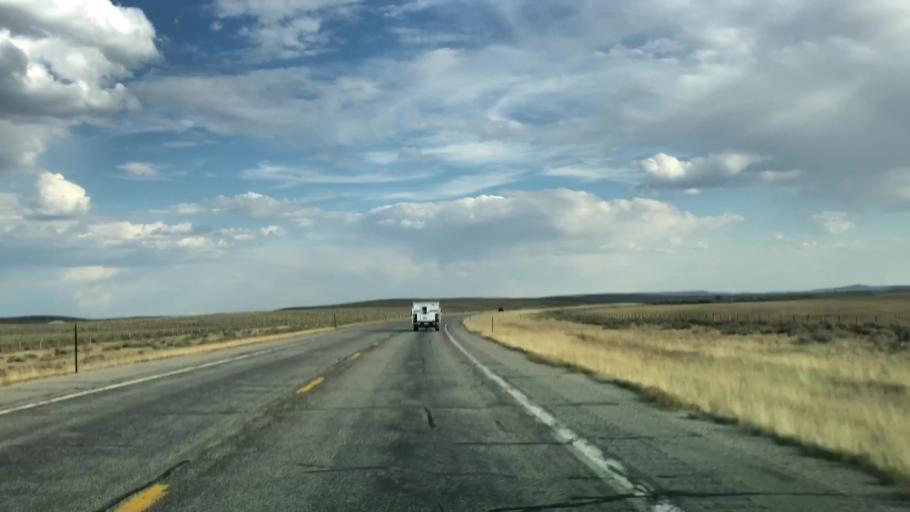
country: US
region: Wyoming
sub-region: Sublette County
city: Pinedale
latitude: 43.0338
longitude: -110.1304
